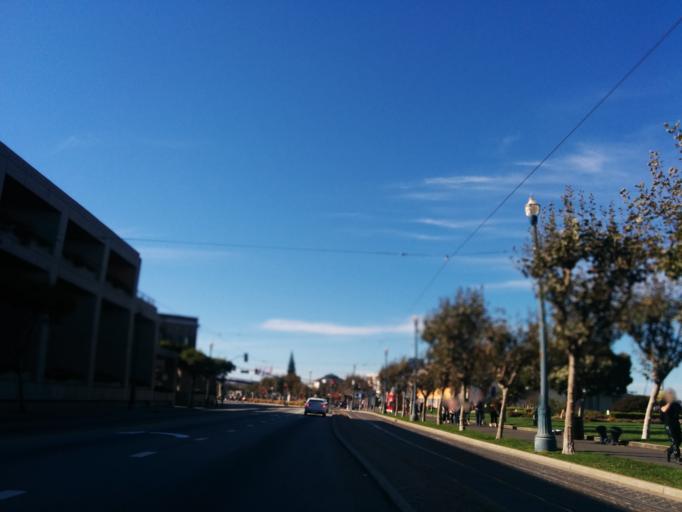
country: US
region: California
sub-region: San Francisco County
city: San Francisco
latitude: 37.8078
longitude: -122.4081
